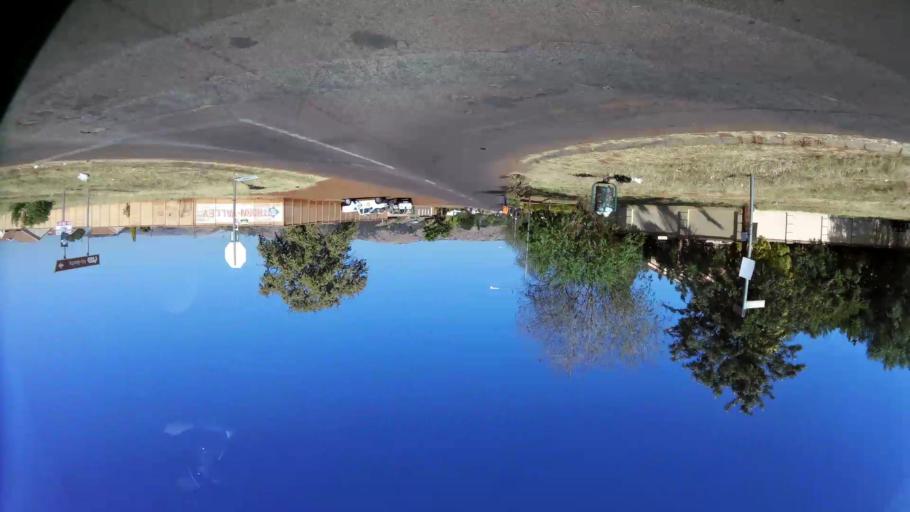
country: ZA
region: North-West
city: Ga-Rankuwa
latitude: -25.6619
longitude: 28.0939
